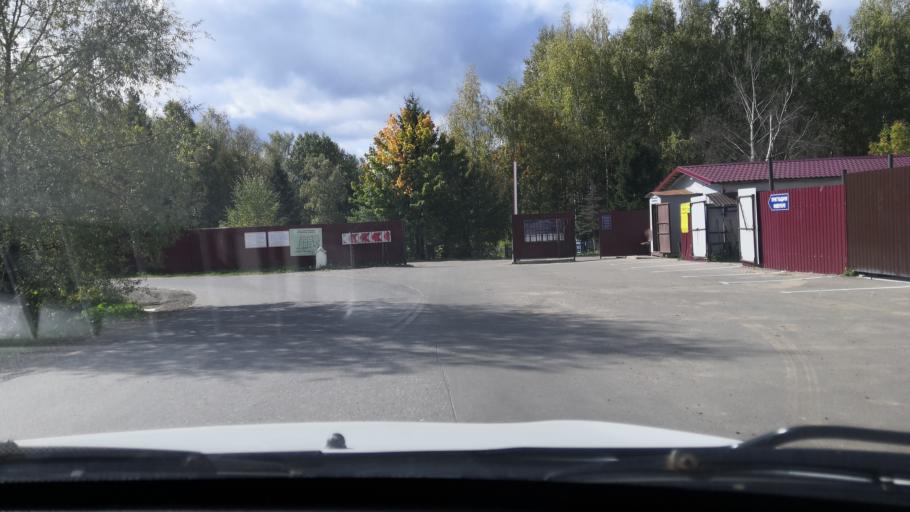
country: RU
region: Moskovskaya
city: Povarovo
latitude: 56.0655
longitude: 37.0418
